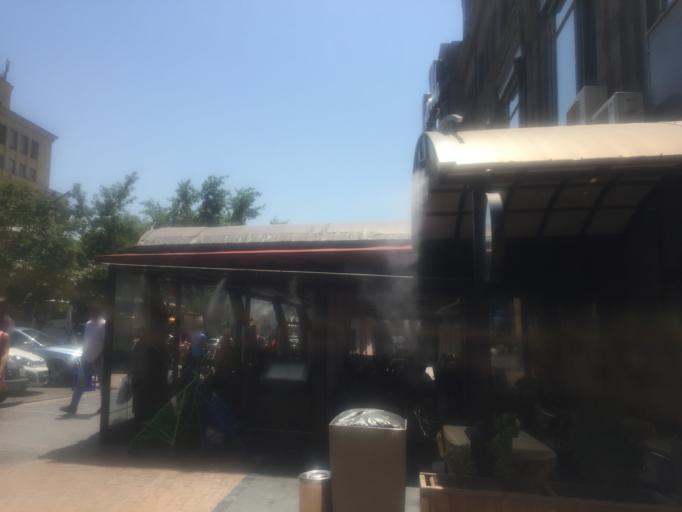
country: AM
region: Yerevan
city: Yerevan
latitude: 40.1799
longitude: 44.5142
